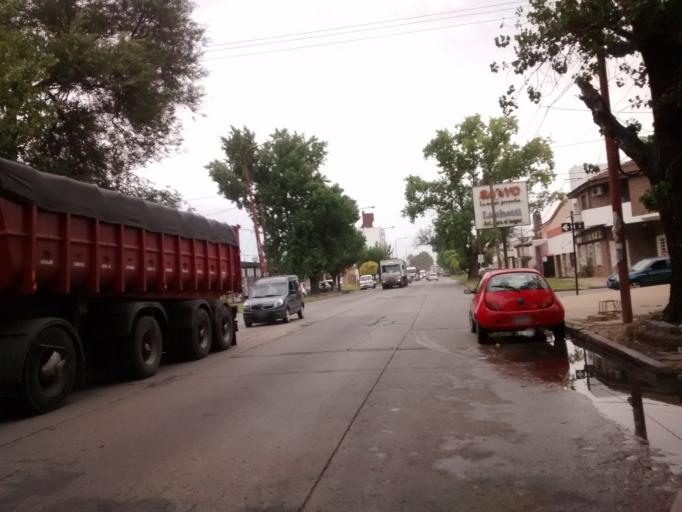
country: AR
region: Buenos Aires
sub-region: Partido de La Plata
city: La Plata
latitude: -34.8925
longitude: -57.9849
